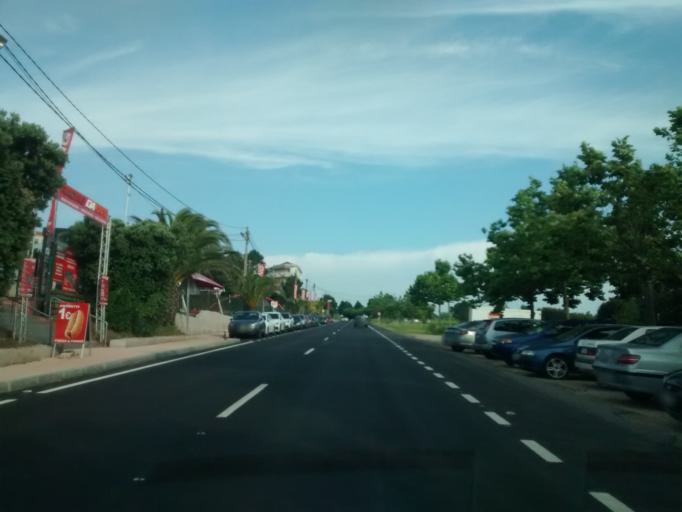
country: ES
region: Galicia
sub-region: Provincia de Pontevedra
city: Sanxenxo
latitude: 42.4151
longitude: -8.8669
